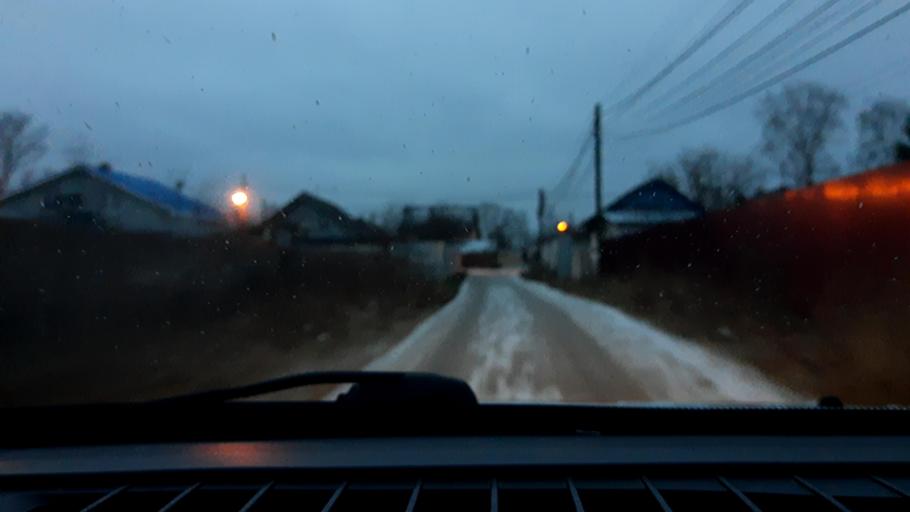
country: RU
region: Nizjnij Novgorod
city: Gorbatovka
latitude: 56.3878
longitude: 43.7519
